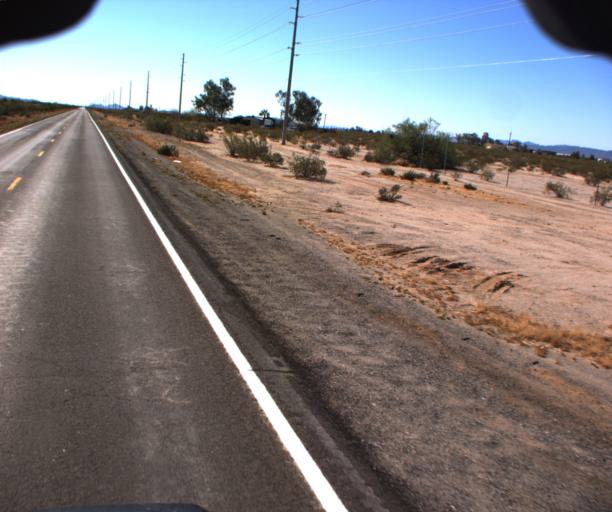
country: US
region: Arizona
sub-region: La Paz County
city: Salome
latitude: 33.8687
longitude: -113.9289
